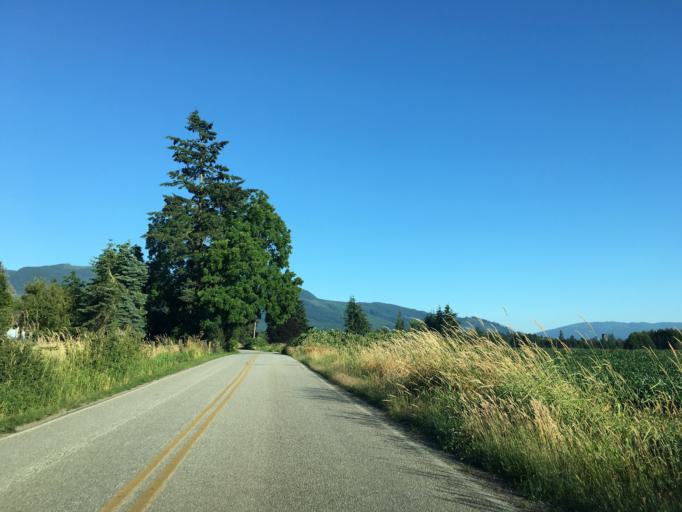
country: US
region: Washington
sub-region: Whatcom County
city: Nooksack
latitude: 48.9490
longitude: -122.3162
